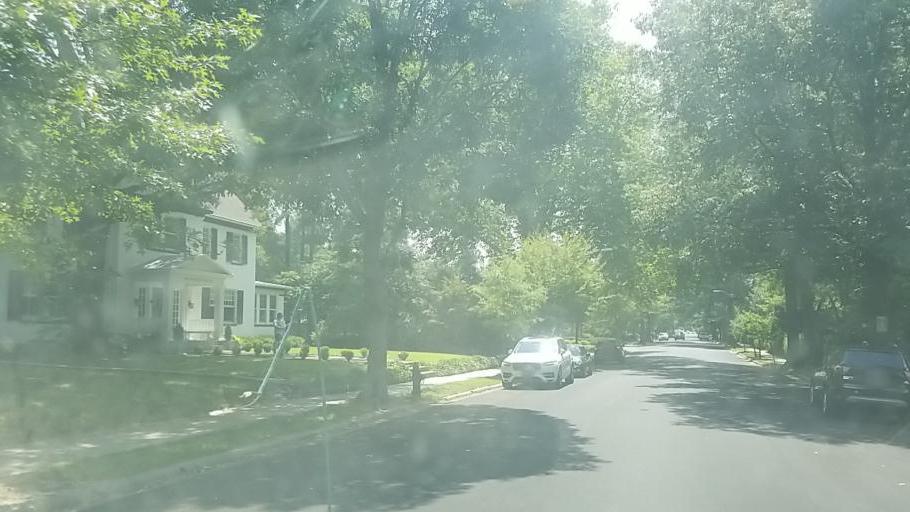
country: US
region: Maryland
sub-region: Talbot County
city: Easton
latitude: 38.7700
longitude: -76.0743
